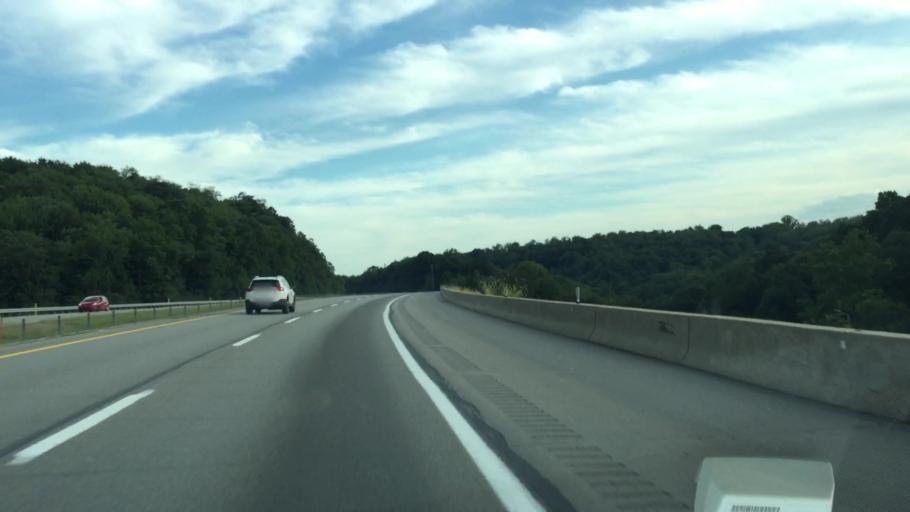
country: US
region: Pennsylvania
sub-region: Allegheny County
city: Franklin Park
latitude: 40.5701
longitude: -80.0904
